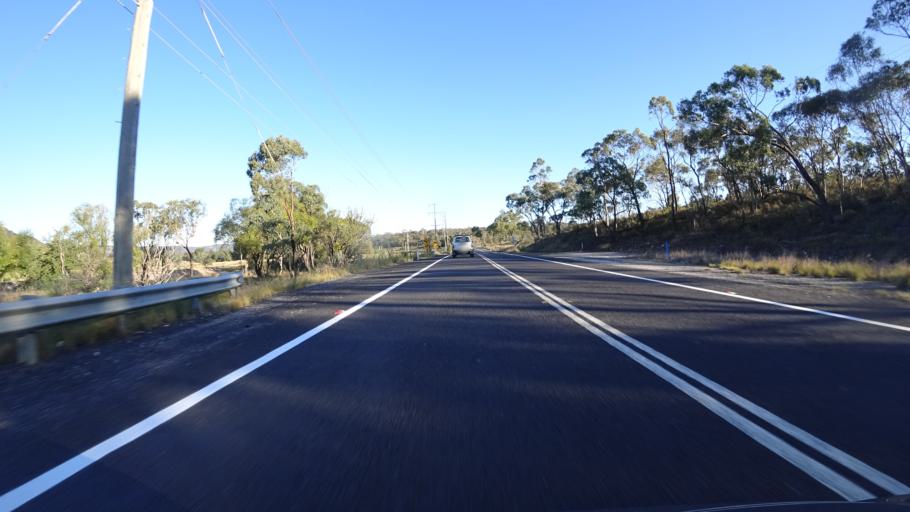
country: AU
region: New South Wales
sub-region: Lithgow
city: Portland
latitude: -33.3609
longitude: 150.0575
